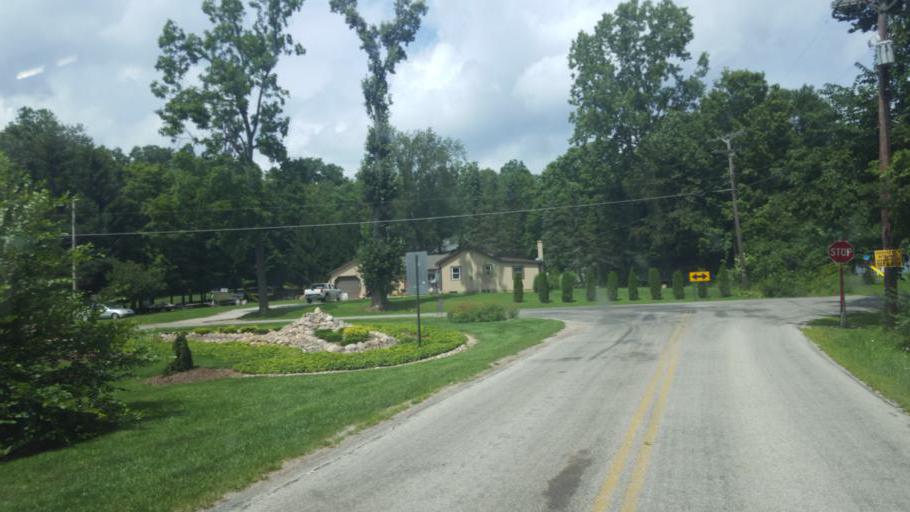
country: US
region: Ohio
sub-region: Richland County
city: Ontario
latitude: 40.7439
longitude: -82.6392
